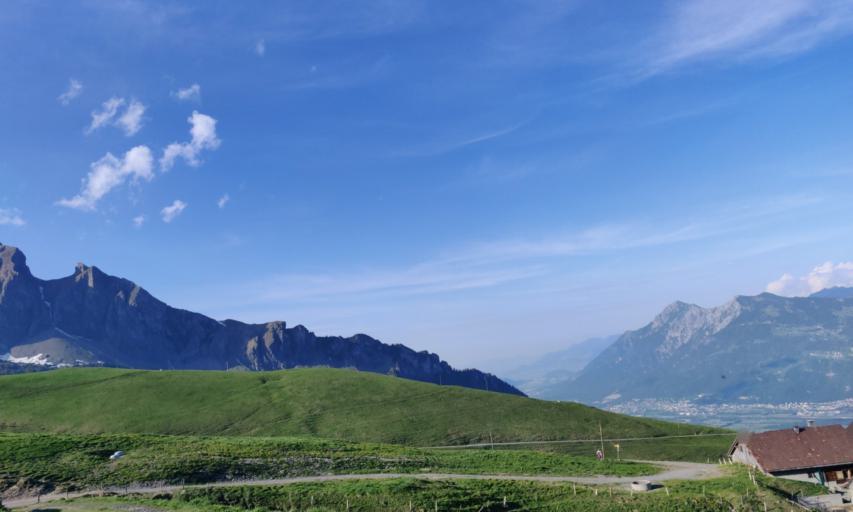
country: CH
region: Saint Gallen
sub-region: Wahlkreis Sarganserland
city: Sargans
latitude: 47.0752
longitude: 9.4314
